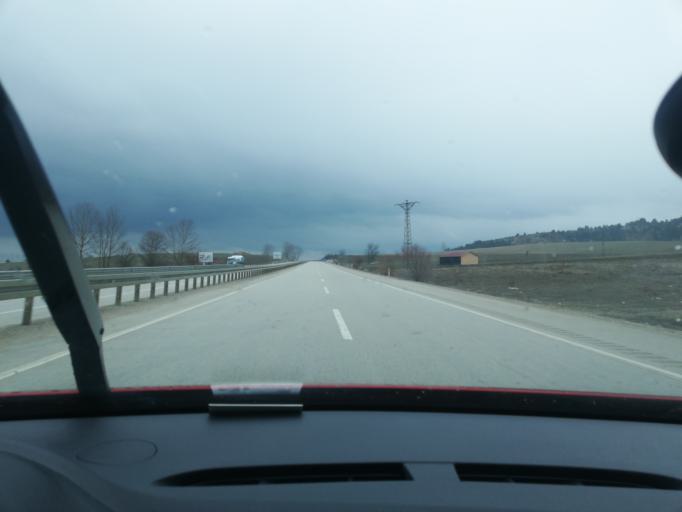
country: TR
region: Kastamonu
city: Seydiler
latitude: 41.6136
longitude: 33.7287
